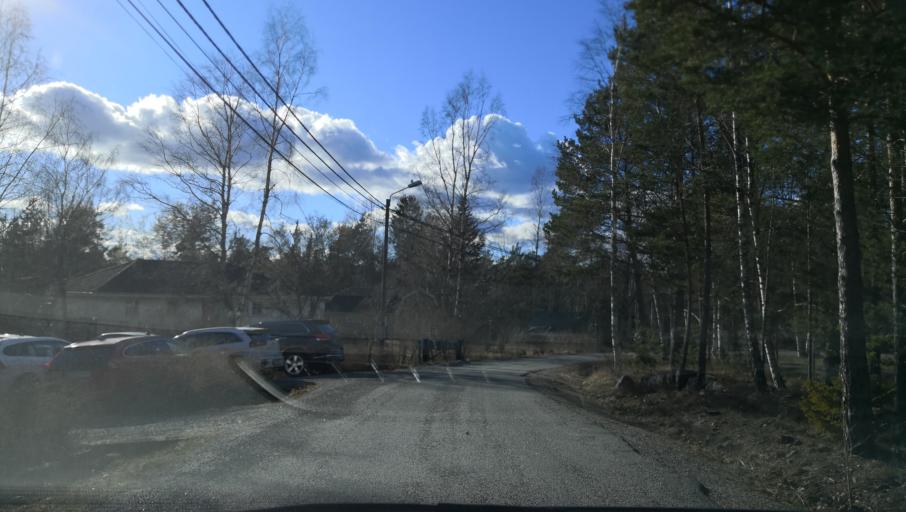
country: SE
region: Stockholm
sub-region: Varmdo Kommun
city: Hemmesta
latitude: 59.2449
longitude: 18.5168
